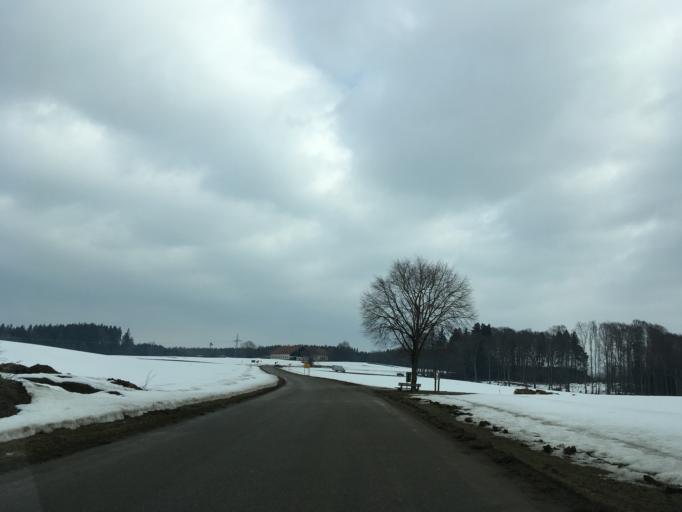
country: DE
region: Bavaria
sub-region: Upper Bavaria
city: Bad Endorf
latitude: 47.9077
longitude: 12.3169
